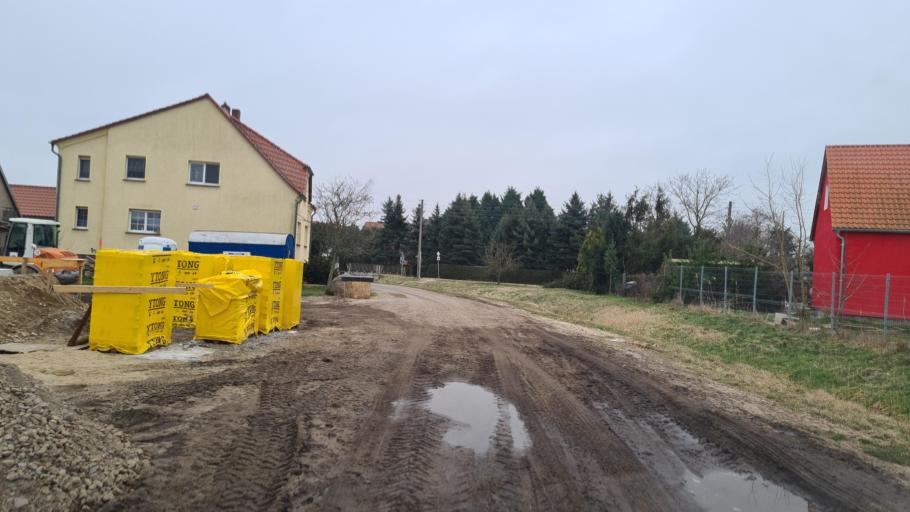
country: DE
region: Brandenburg
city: Herzberg
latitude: 51.6995
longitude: 13.1723
